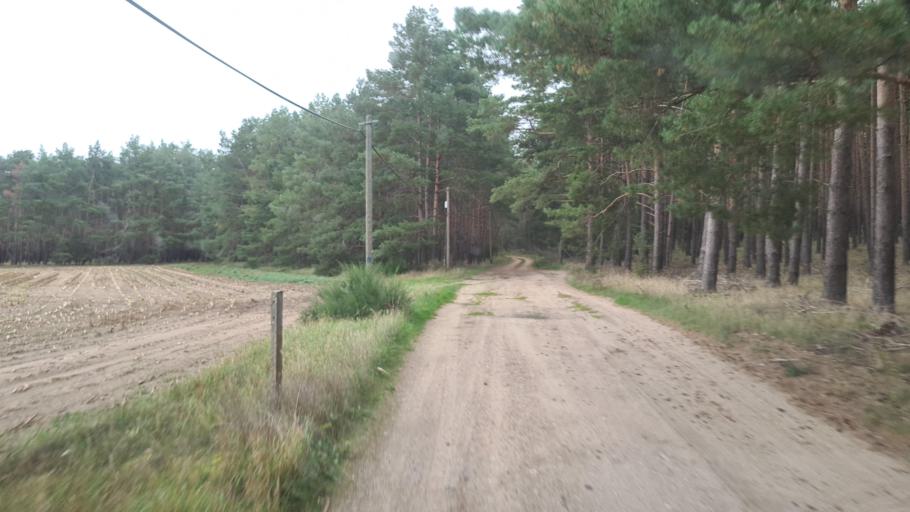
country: DE
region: Brandenburg
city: Golssen
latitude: 51.9524
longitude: 13.5730
